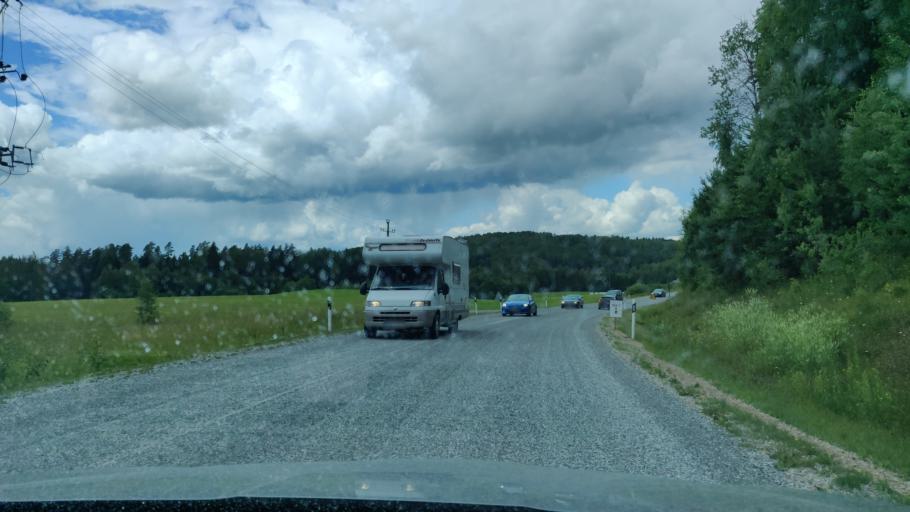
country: EE
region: Vorumaa
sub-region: Antsla vald
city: Vana-Antsla
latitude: 58.0385
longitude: 26.5562
